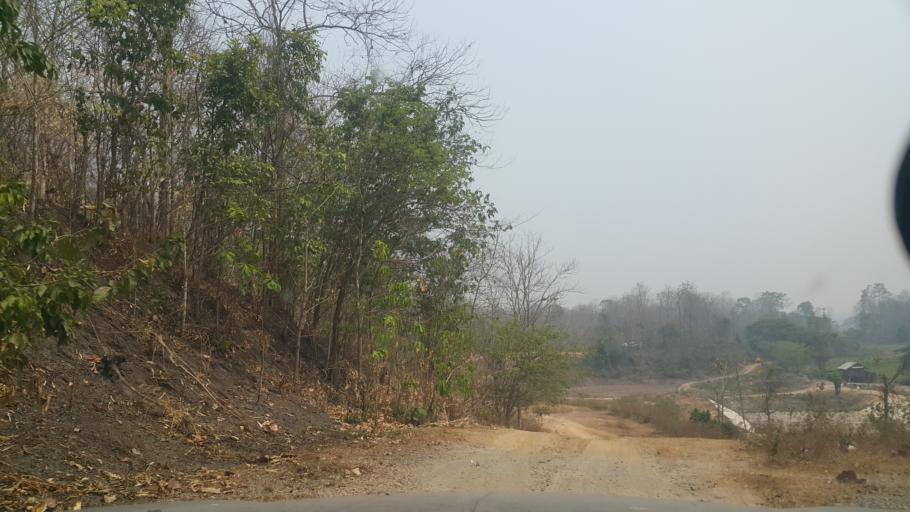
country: TH
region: Lampang
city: Hang Chat
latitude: 18.3222
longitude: 99.2438
